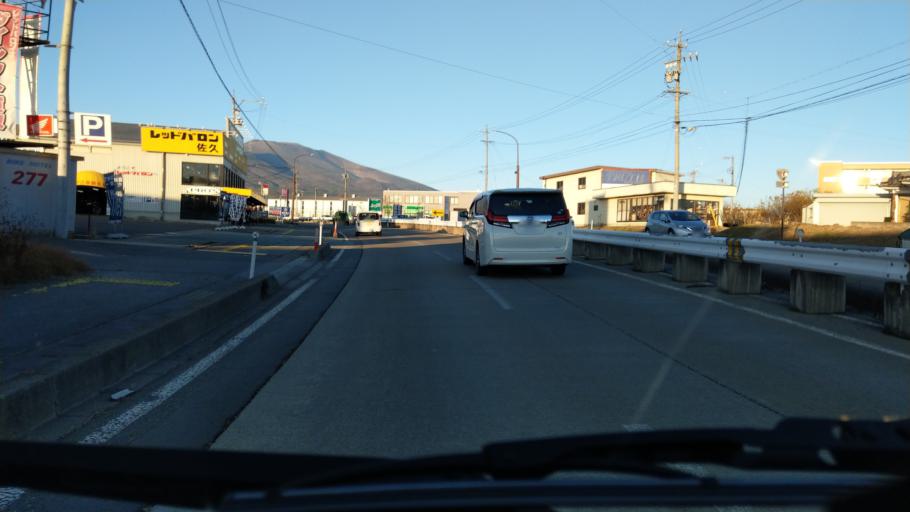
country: JP
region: Nagano
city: Komoro
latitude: 36.2850
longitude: 138.4740
